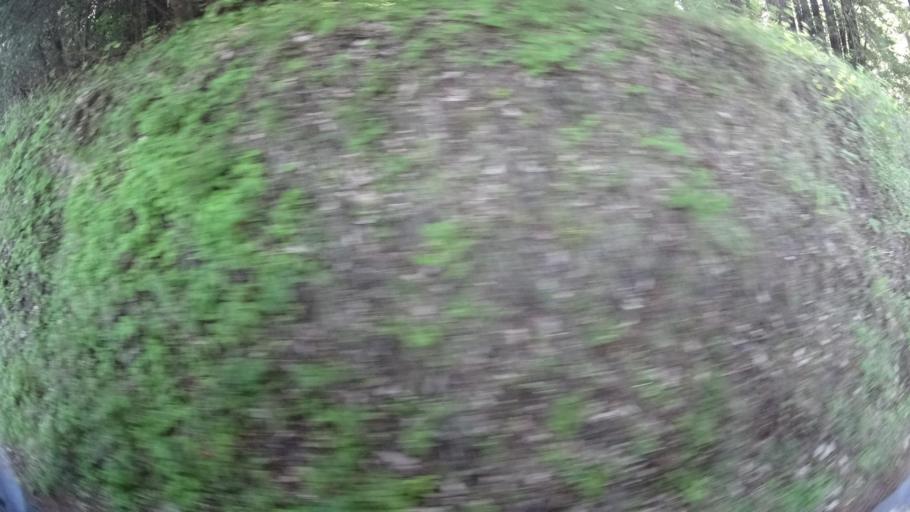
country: US
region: California
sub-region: Humboldt County
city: Rio Dell
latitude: 40.4522
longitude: -123.9869
